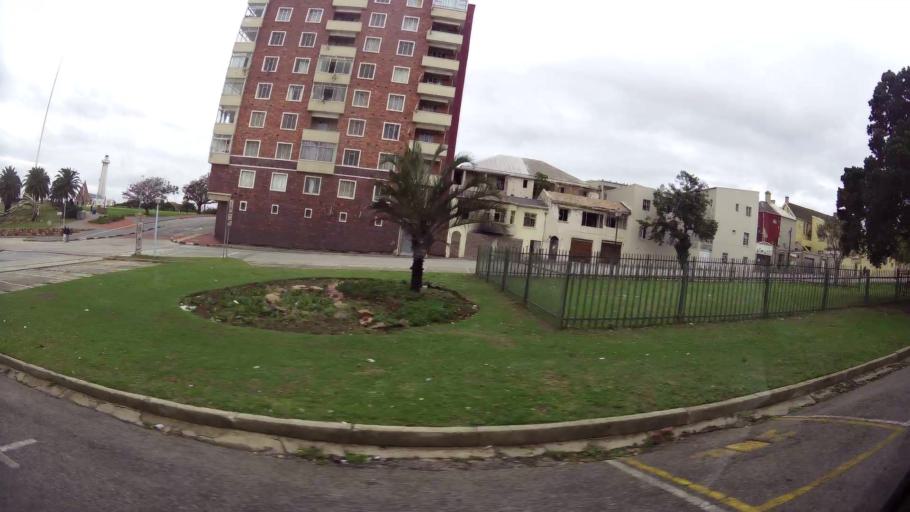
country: ZA
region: Eastern Cape
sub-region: Nelson Mandela Bay Metropolitan Municipality
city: Port Elizabeth
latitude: -33.9612
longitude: 25.6183
